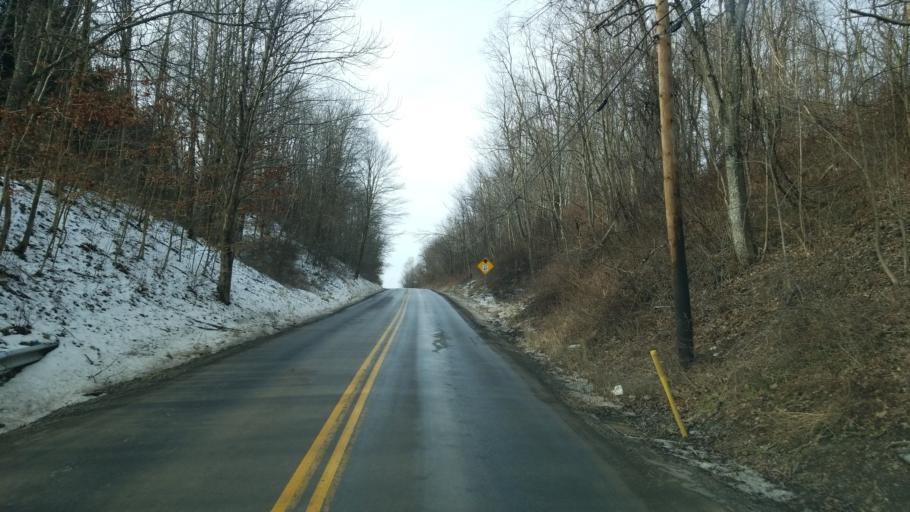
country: US
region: Pennsylvania
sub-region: Indiana County
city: Johnsonburg
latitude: 40.8384
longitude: -78.8560
